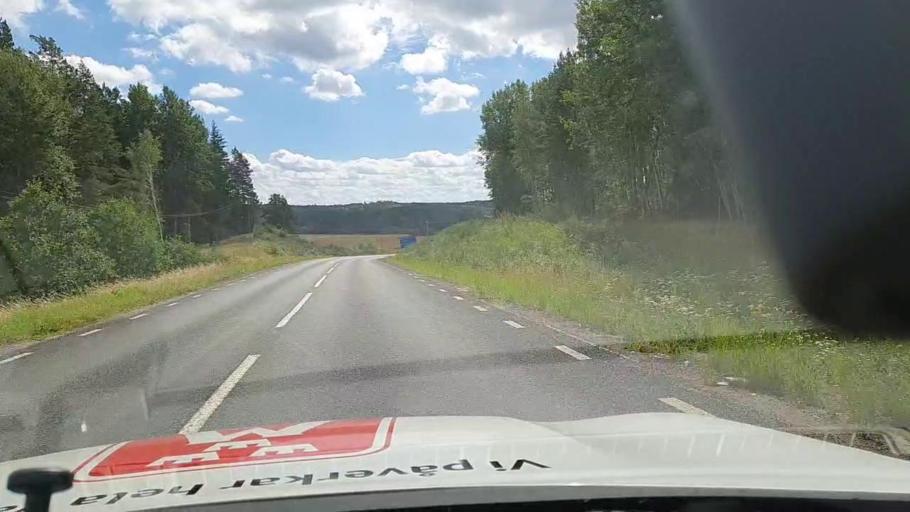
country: SE
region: Soedermanland
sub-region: Nykopings Kommun
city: Olstorp
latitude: 58.7516
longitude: 16.6162
